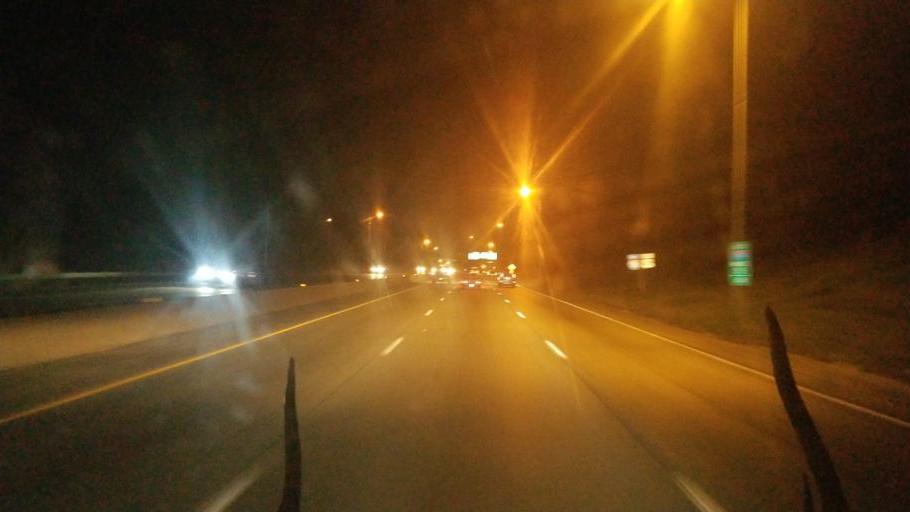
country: US
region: Missouri
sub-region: Jackson County
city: Kansas City
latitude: 39.0815
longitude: -94.5406
